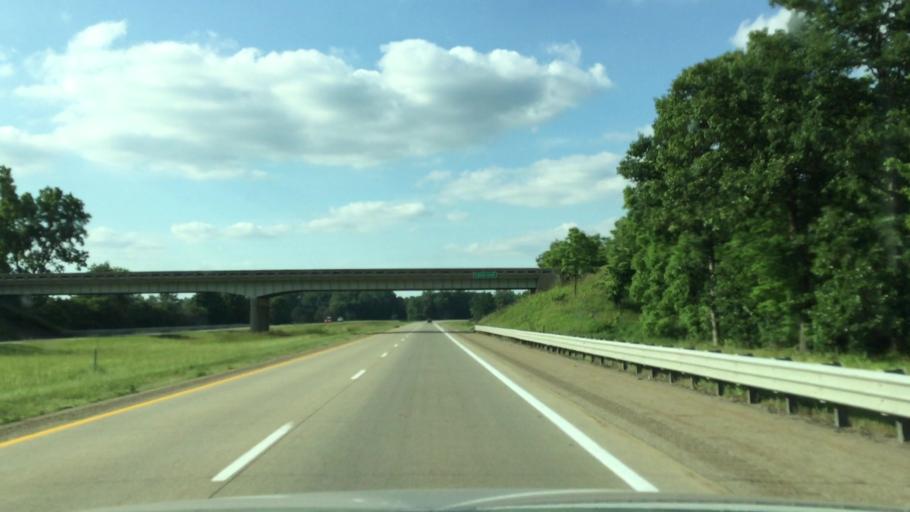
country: US
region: Michigan
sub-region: Calhoun County
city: Marshall
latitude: 42.1303
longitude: -84.9953
